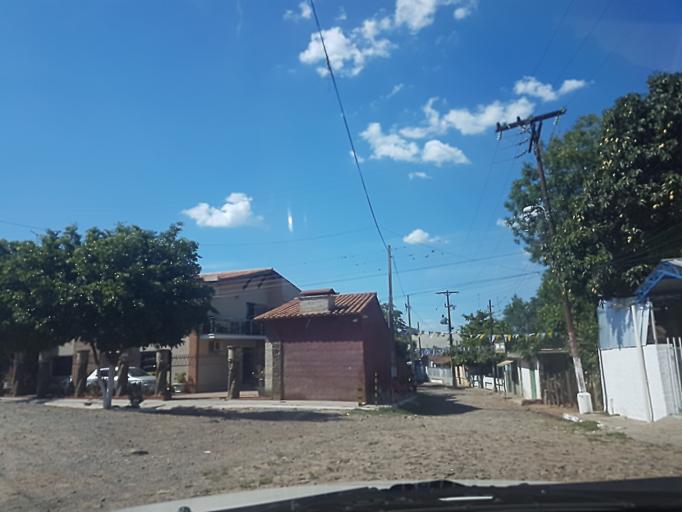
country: PY
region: Central
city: Colonia Mariano Roque Alonso
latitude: -25.2265
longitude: -57.5677
